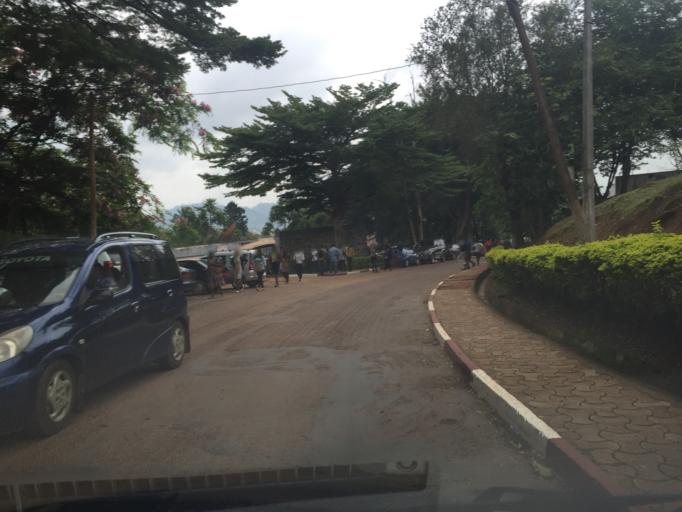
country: CM
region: Centre
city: Yaounde
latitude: 3.8568
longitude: 11.5023
